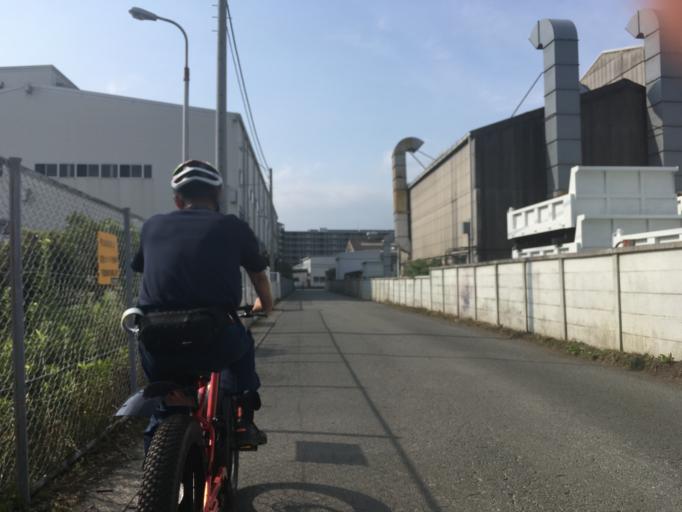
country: JP
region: Kanagawa
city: Minami-rinkan
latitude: 35.4804
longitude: 139.4626
